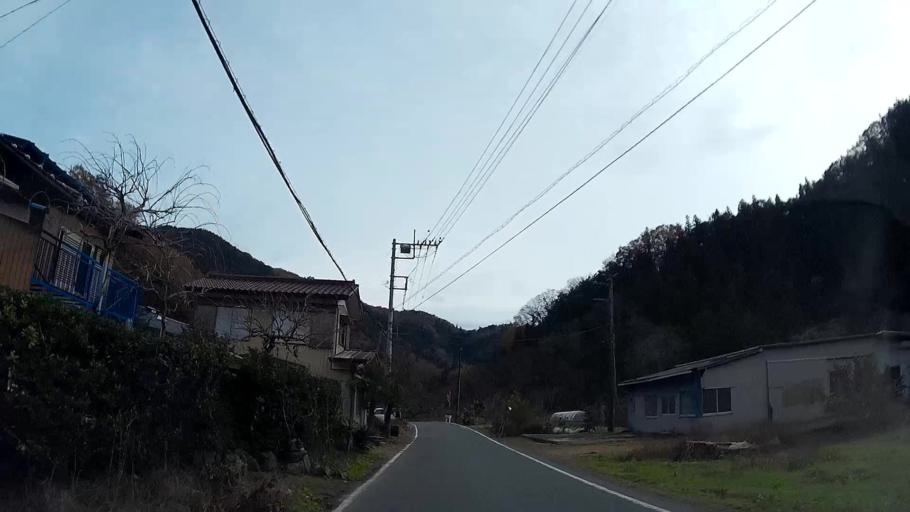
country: JP
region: Saitama
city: Chichibu
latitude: 36.0588
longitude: 138.9734
